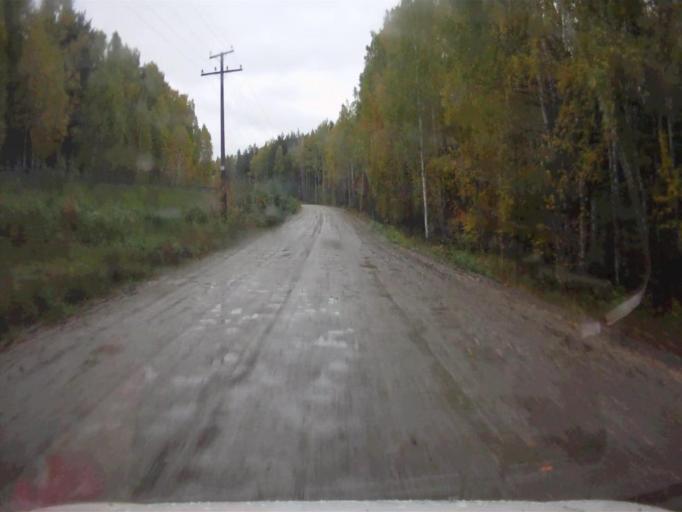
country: RU
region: Chelyabinsk
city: Kyshtym
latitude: 55.8037
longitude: 60.4800
